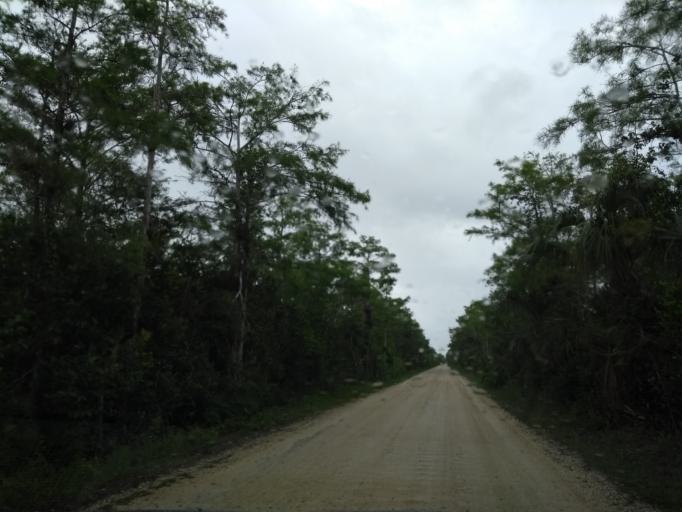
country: US
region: Florida
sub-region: Miami-Dade County
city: The Hammocks
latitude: 25.7606
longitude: -80.9987
